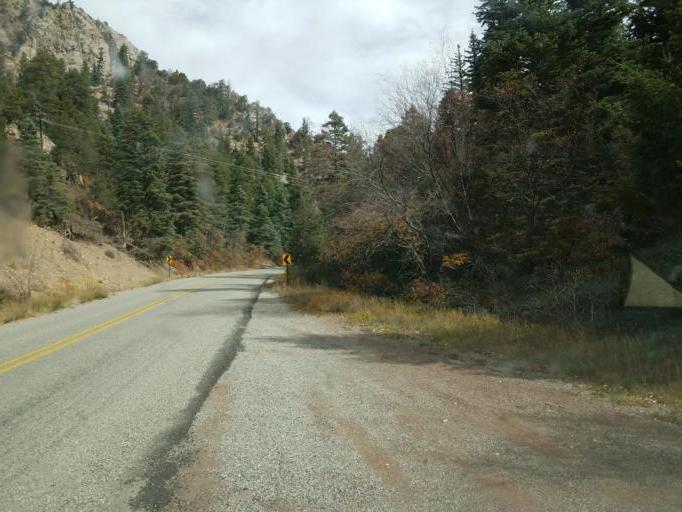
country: US
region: New Mexico
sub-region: Taos County
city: Arroyo Seco
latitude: 36.5505
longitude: -105.5444
